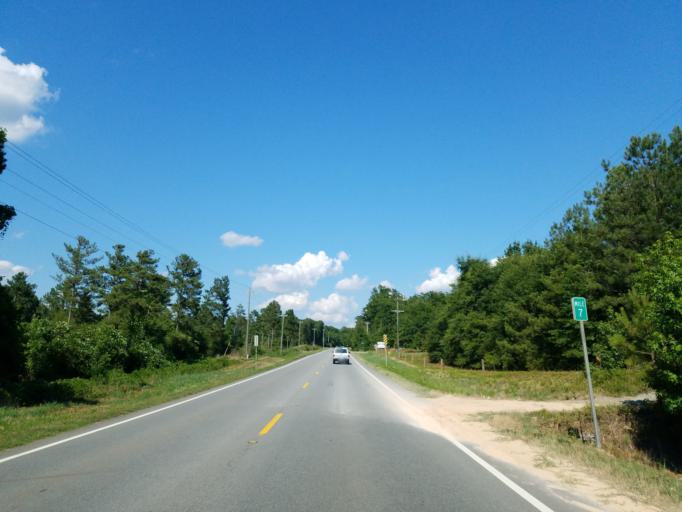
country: US
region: Georgia
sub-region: Peach County
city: Fort Valley
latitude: 32.5556
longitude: -83.8567
